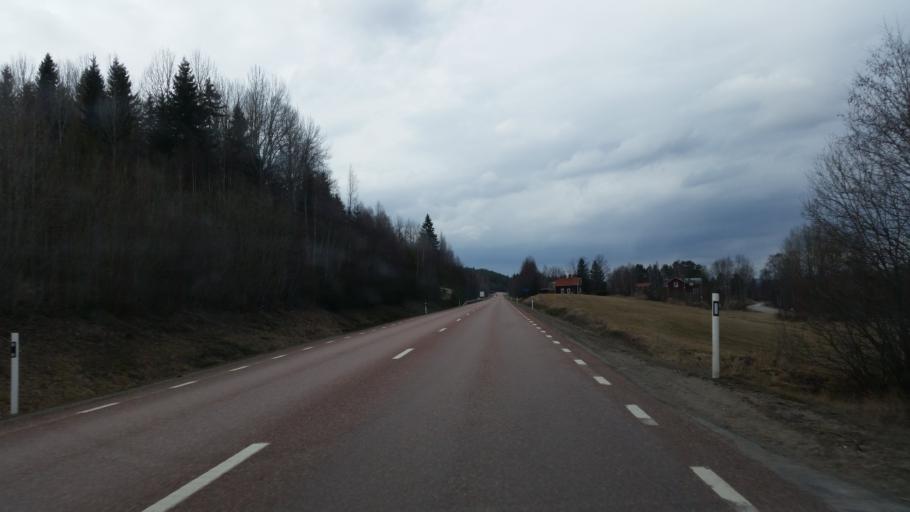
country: SE
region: Gaevleborg
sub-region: Ljusdals Kommun
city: Jaervsoe
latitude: 61.7292
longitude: 16.1665
